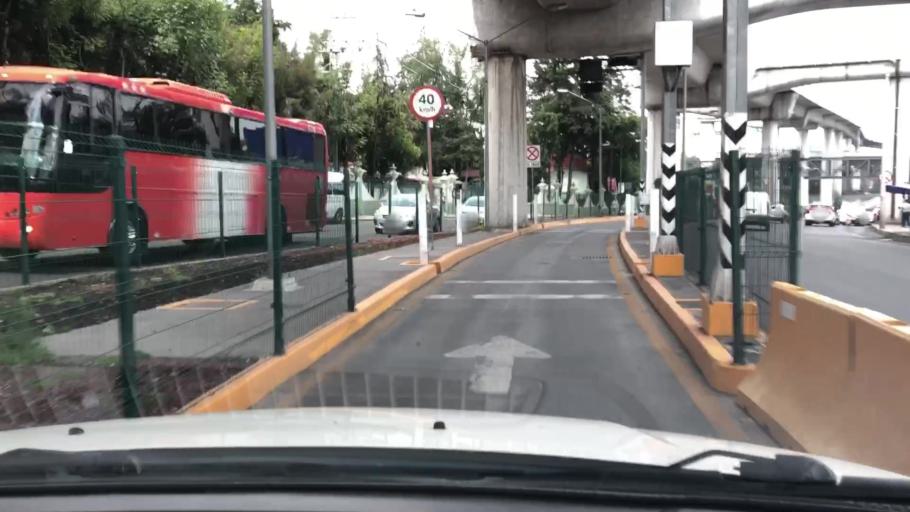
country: MX
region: Mexico City
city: Miguel Hidalgo
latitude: 19.4437
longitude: -99.2207
